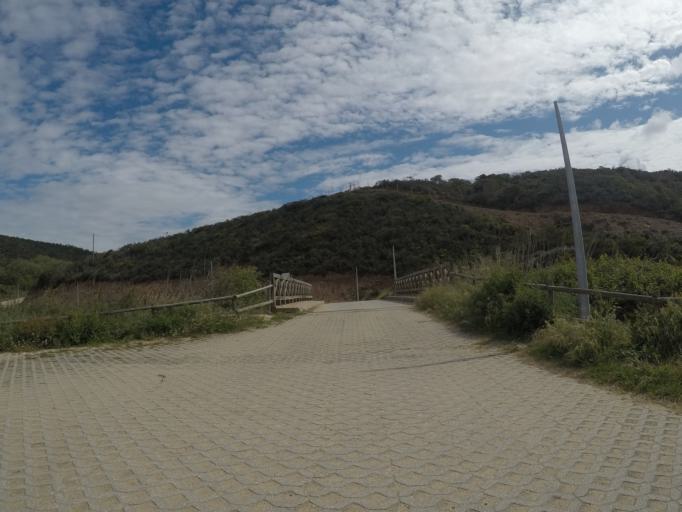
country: PT
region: Beja
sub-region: Odemira
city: Sao Teotonio
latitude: 37.4996
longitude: -8.7900
